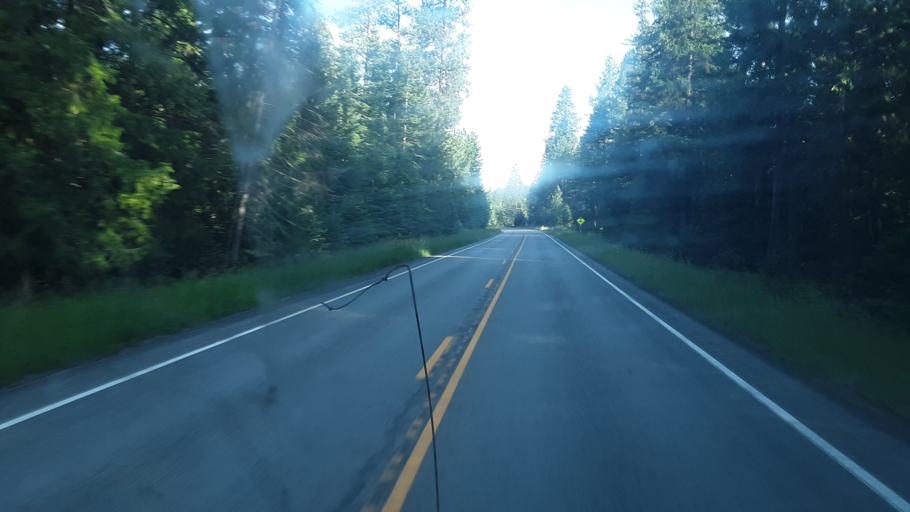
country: US
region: Idaho
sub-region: Boundary County
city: Bonners Ferry
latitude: 48.6007
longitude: -116.0021
